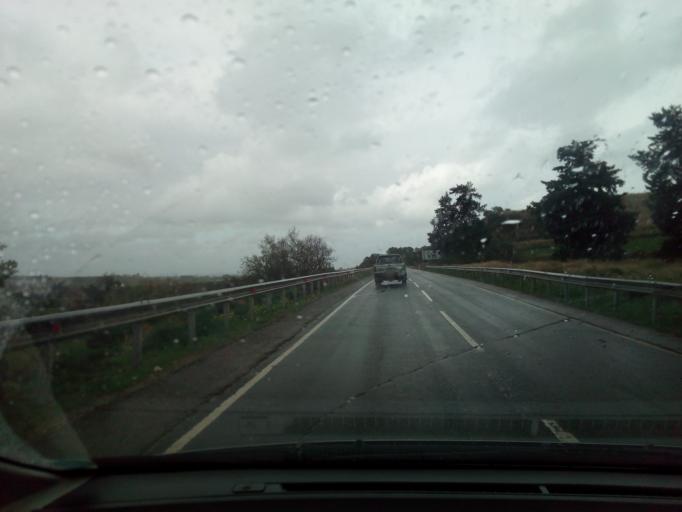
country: CY
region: Pafos
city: Polis
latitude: 35.0099
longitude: 32.4369
